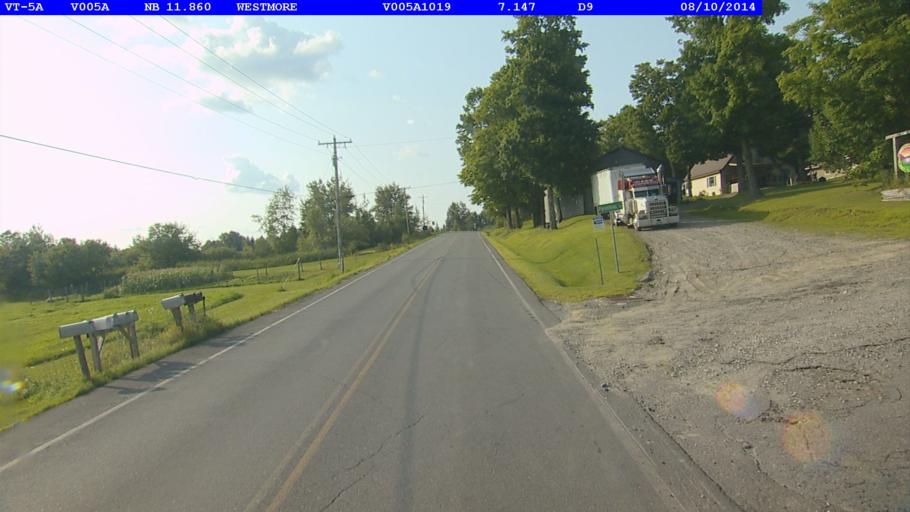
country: US
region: Vermont
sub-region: Orleans County
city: Newport
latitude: 44.7864
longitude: -72.0759
